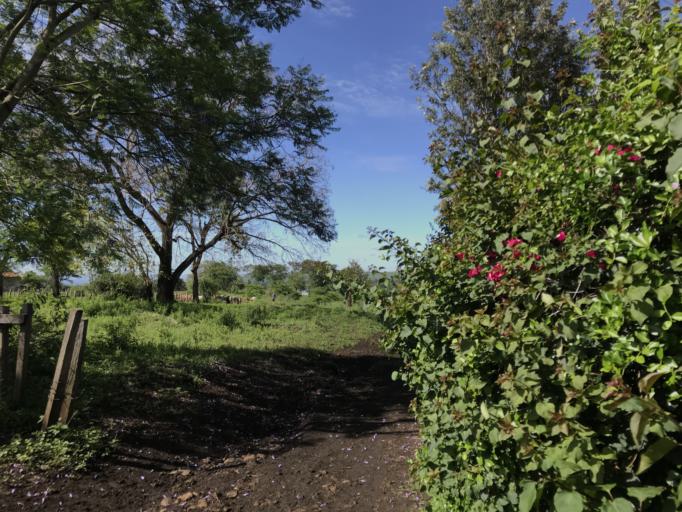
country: TZ
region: Arusha
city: Usa River
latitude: -3.3916
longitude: 36.7977
